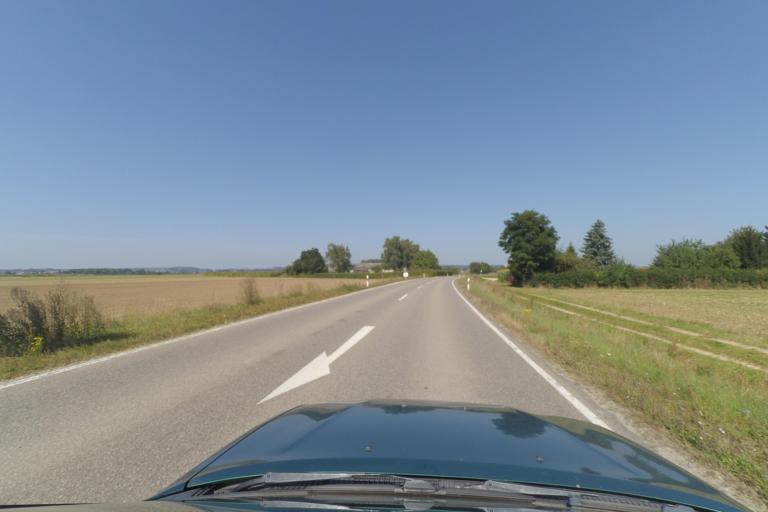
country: DE
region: Bavaria
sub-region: Swabia
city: Lauingen
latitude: 48.5809
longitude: 10.4085
